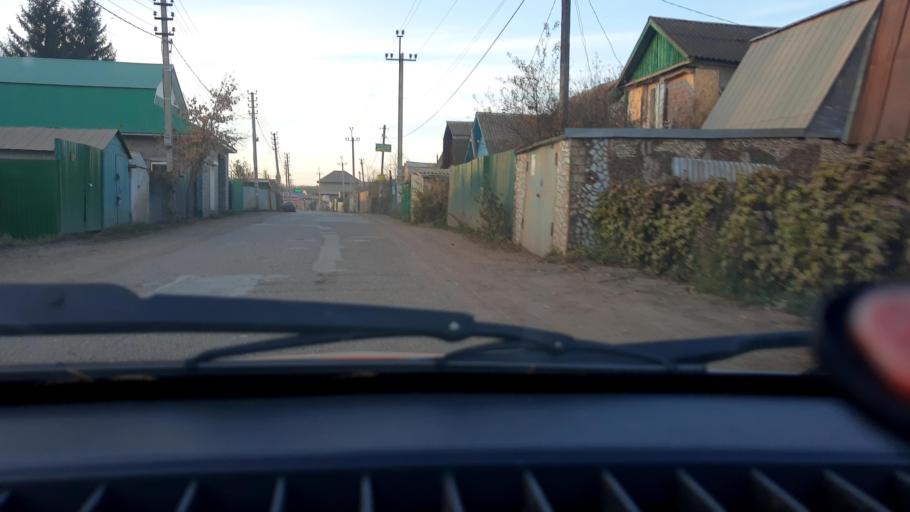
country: RU
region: Bashkortostan
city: Ufa
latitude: 54.6933
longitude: 55.9009
